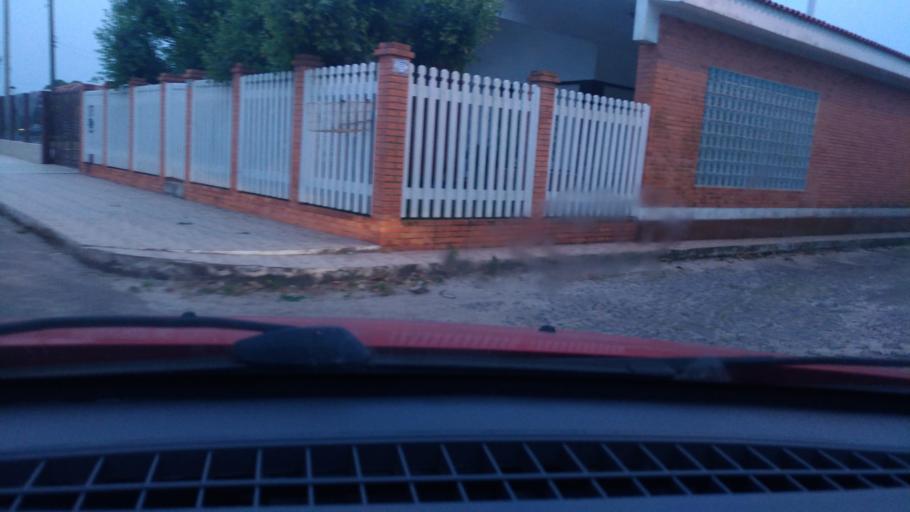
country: BR
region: Rio Grande do Sul
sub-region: Capao Da Canoa
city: Capao da Canoa
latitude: -29.8484
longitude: -50.0635
